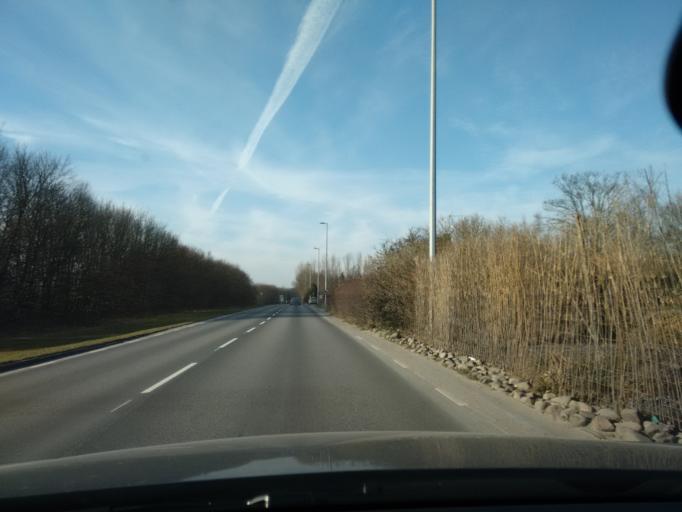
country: SE
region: Skane
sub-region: Lunds Kommun
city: Lund
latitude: 55.7254
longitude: 13.1817
